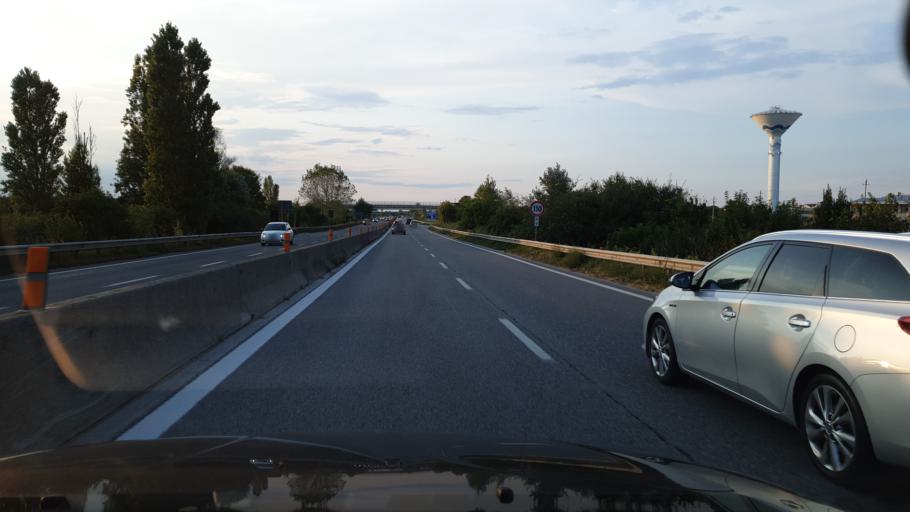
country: IT
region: Emilia-Romagna
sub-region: Forli-Cesena
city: Gatteo a Mare
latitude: 44.1708
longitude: 12.4212
